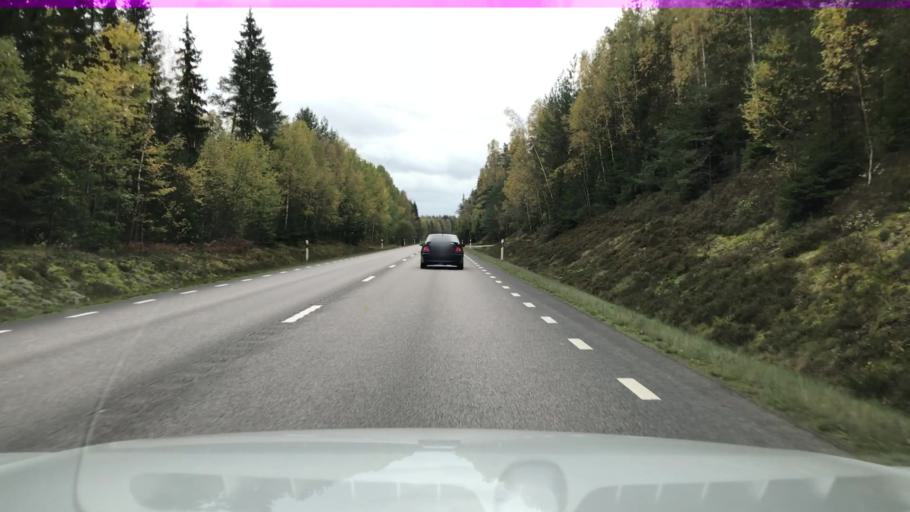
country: SE
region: Kalmar
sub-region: Hultsfreds Kommun
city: Hultsfred
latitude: 57.5469
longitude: 15.8457
